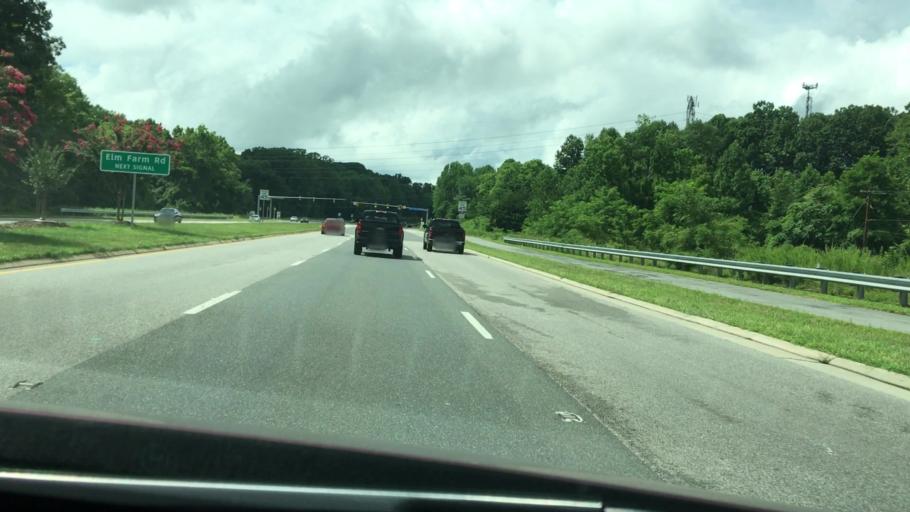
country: US
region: Virginia
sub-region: Prince William County
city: Dale City
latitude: 38.6585
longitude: -77.3224
